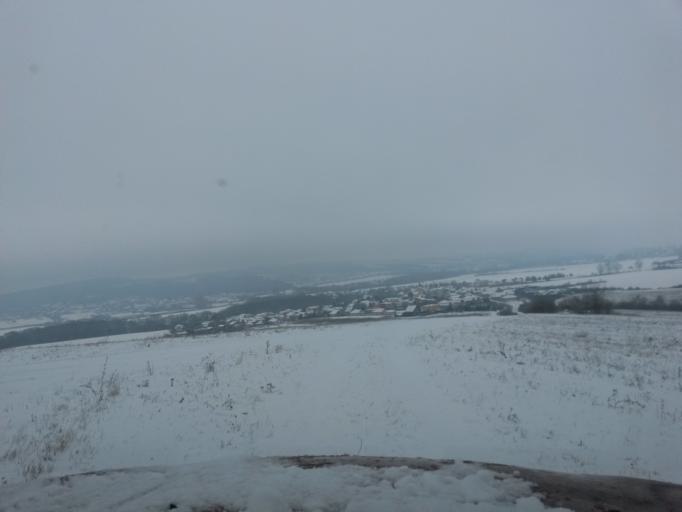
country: SK
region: Kosicky
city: Kosice
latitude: 48.7140
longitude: 21.3224
